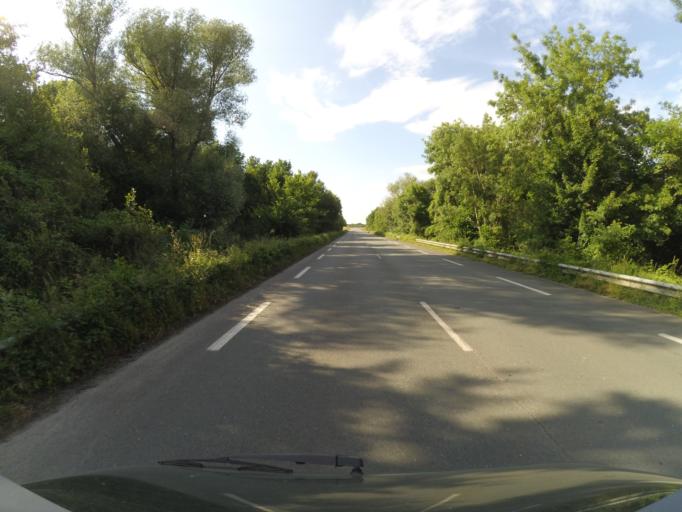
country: FR
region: Poitou-Charentes
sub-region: Departement de la Charente-Maritime
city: Saint-Agnant
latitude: 45.8285
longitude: -0.9359
